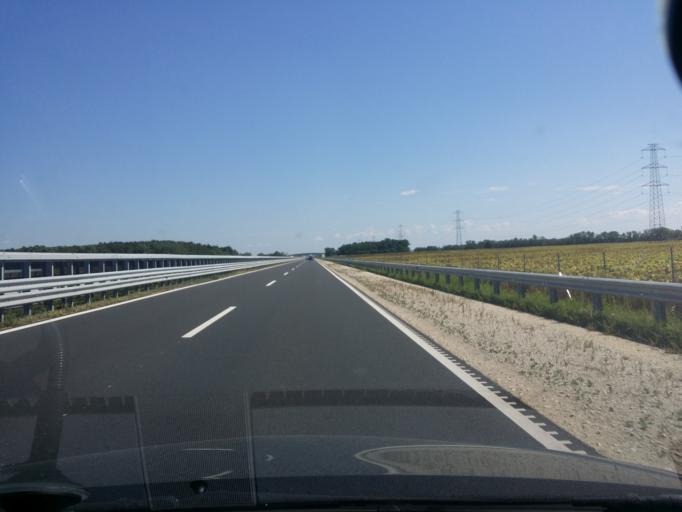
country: HU
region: Vas
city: Repcelak
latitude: 47.3703
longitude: 16.9349
